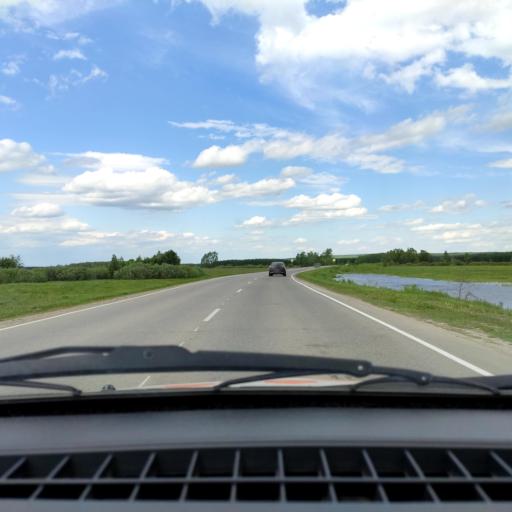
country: RU
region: Bashkortostan
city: Iglino
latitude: 54.9640
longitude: 56.4850
